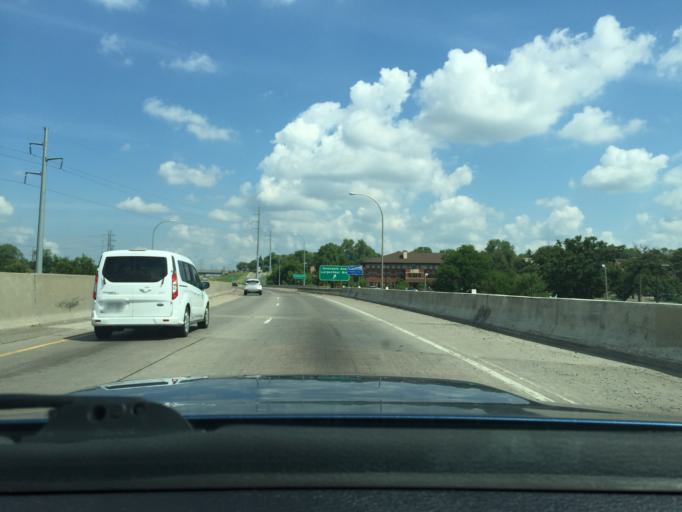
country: US
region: Minnesota
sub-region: Ramsey County
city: Lauderdale
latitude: 44.9871
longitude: -93.2034
